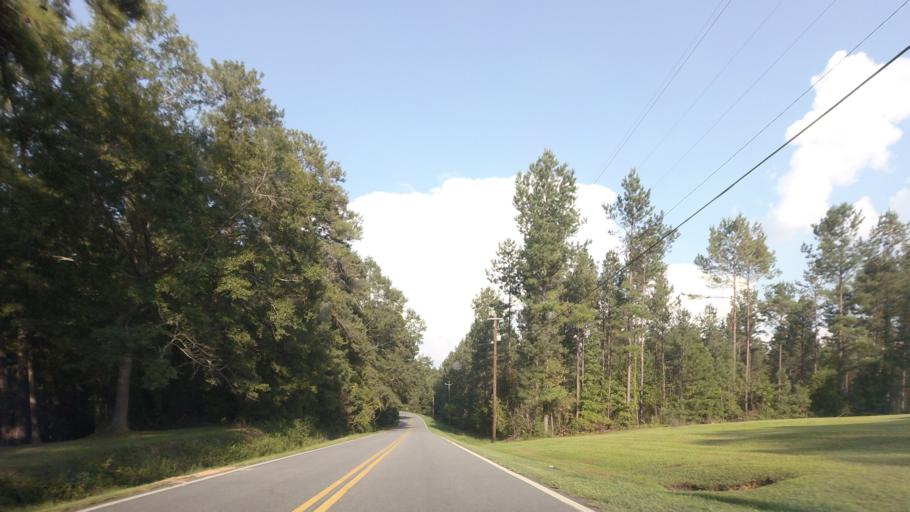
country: US
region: Georgia
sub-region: Bibb County
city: Macon
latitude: 32.8472
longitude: -83.7126
